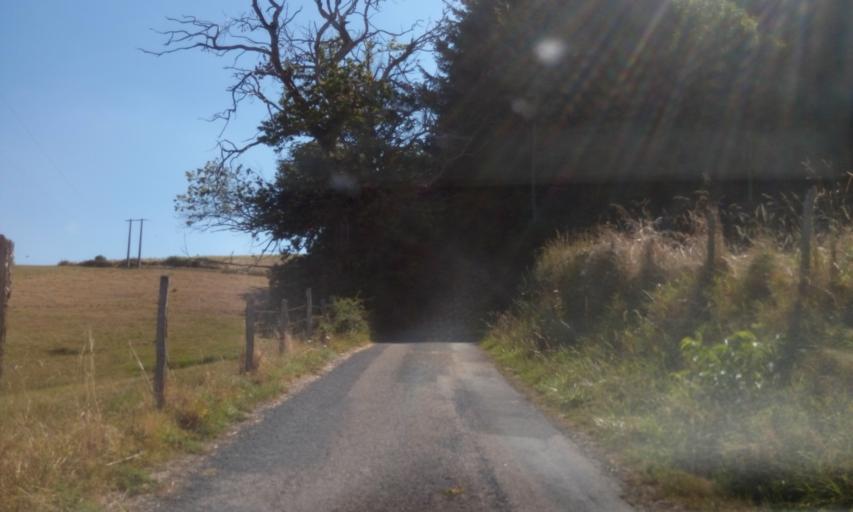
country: FR
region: Rhone-Alpes
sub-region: Departement du Rhone
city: Amplepuis
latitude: 45.9645
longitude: 4.3537
